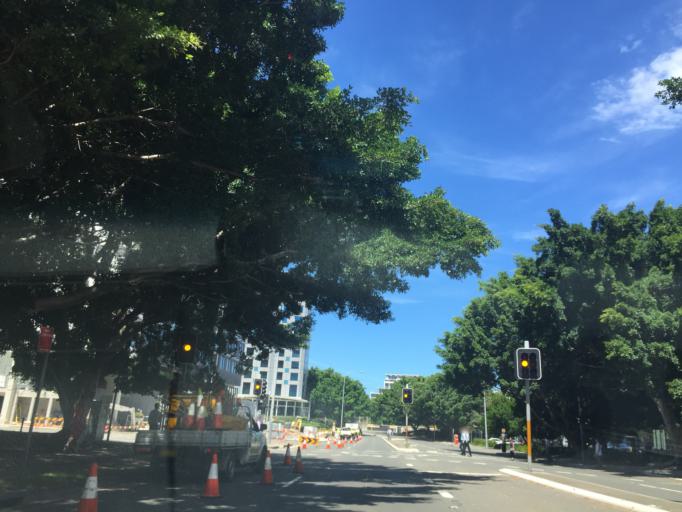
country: AU
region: New South Wales
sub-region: Botany Bay
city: Mascot
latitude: -33.9248
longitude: 151.1873
